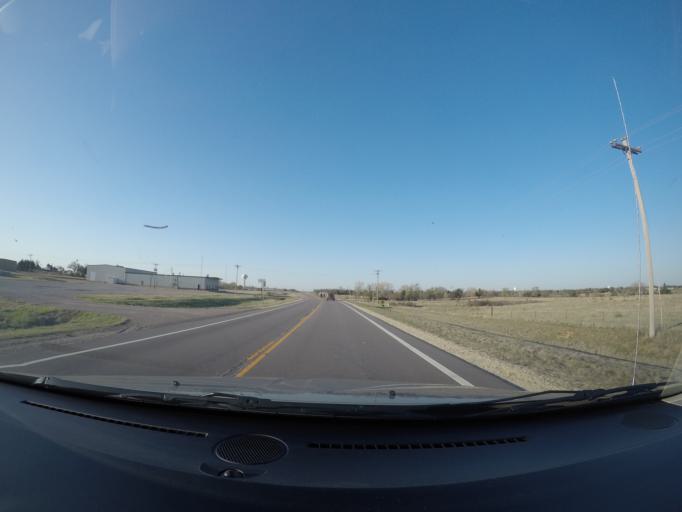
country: US
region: Kansas
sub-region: Pratt County
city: Pratt
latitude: 37.6656
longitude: -98.7163
